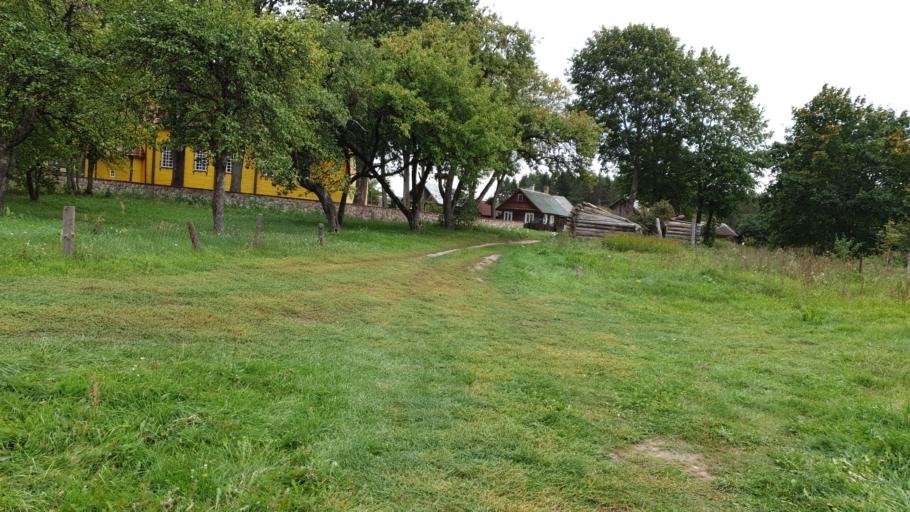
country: LT
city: Grigiskes
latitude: 54.7317
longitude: 25.0429
